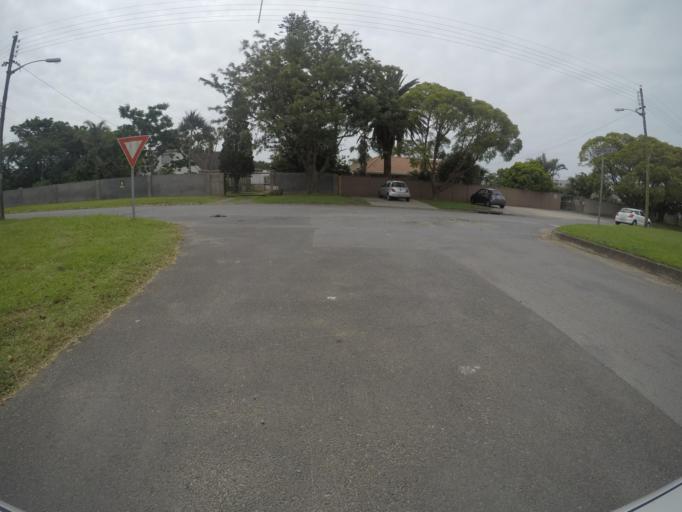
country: ZA
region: Eastern Cape
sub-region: Buffalo City Metropolitan Municipality
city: East London
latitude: -32.9740
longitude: 27.9389
